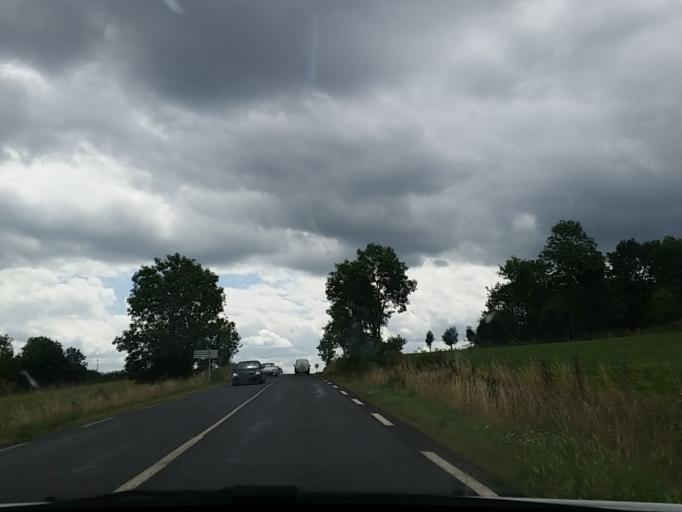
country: FR
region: Auvergne
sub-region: Departement du Cantal
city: Neuveglise
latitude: 44.9499
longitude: 3.0083
